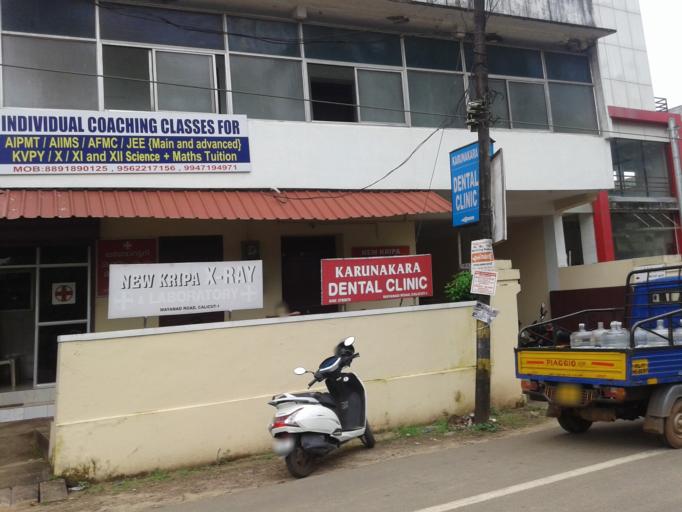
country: IN
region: Kerala
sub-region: Kozhikode
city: Kozhikode
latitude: 11.2631
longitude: 75.7802
